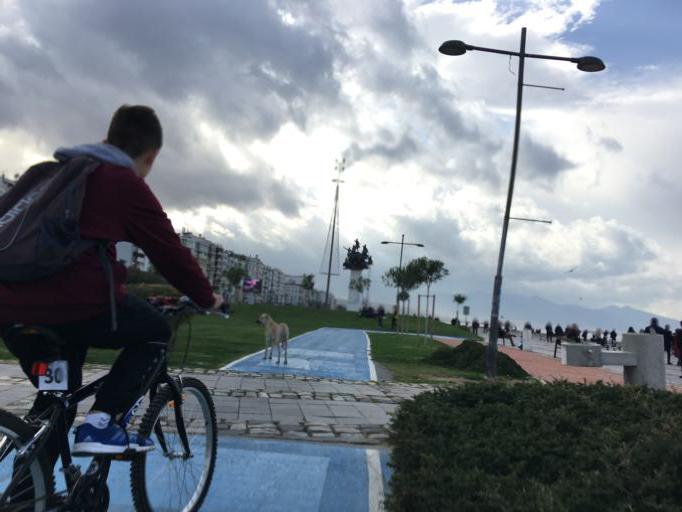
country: TR
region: Izmir
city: Izmir
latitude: 38.4366
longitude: 27.1400
